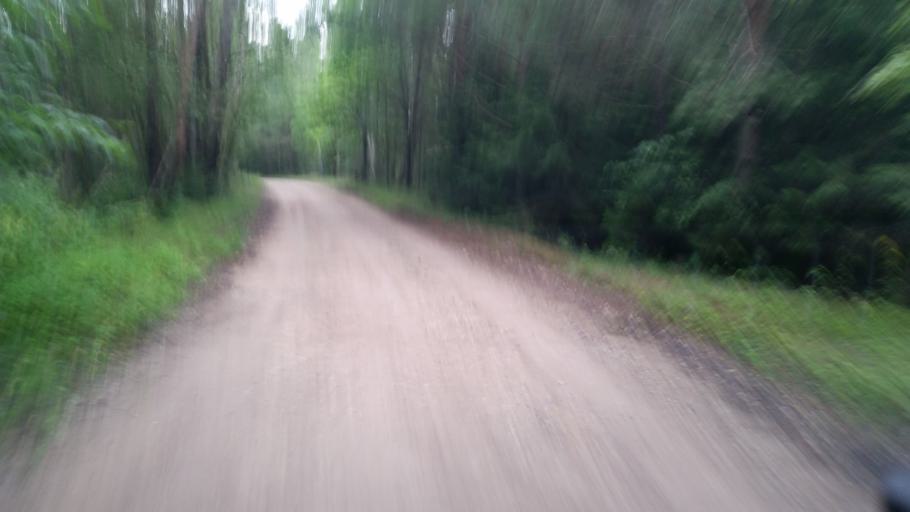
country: LV
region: Vecumnieki
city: Vecumnieki
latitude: 56.4407
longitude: 24.6226
